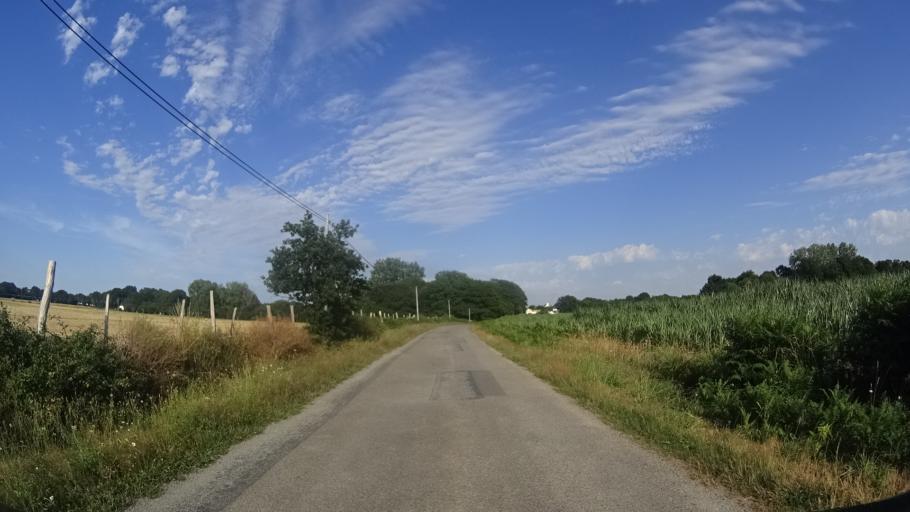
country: FR
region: Brittany
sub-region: Departement du Morbihan
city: Saint-Jean-la-Poterie
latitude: 47.6412
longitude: -2.1409
